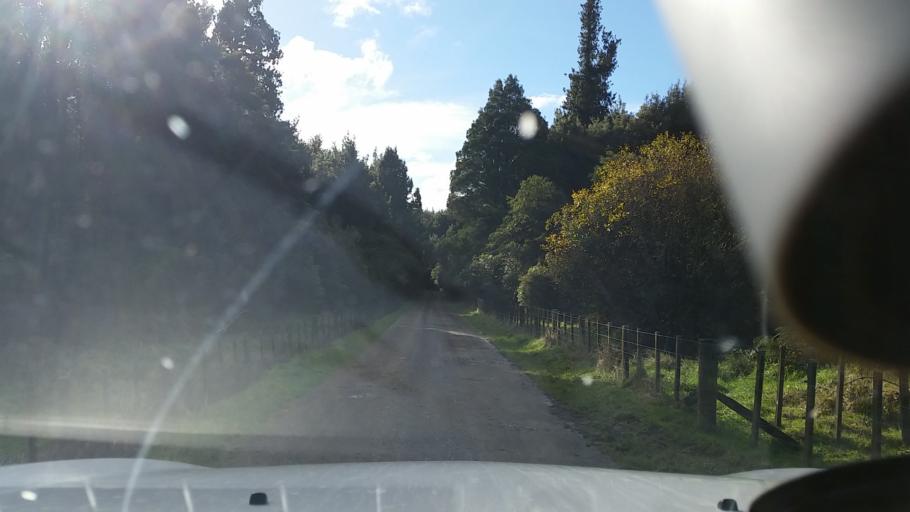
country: NZ
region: Bay of Plenty
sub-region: Rotorua District
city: Rotorua
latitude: -38.1099
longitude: 176.0520
